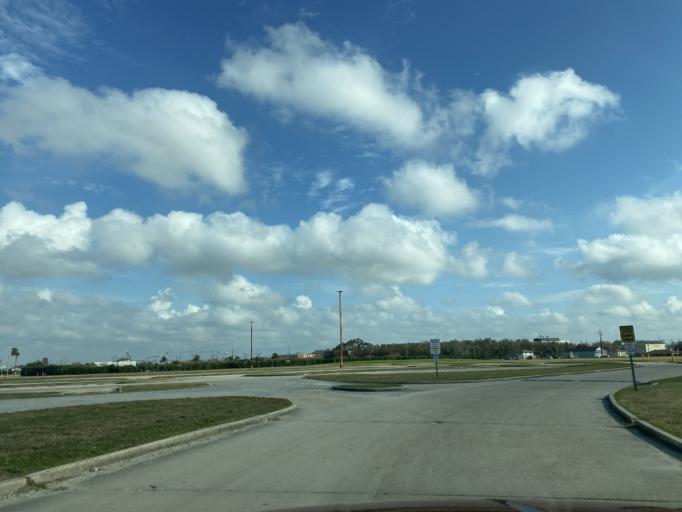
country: US
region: Louisiana
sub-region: Orleans Parish
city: New Orleans
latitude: 30.0287
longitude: -90.0513
